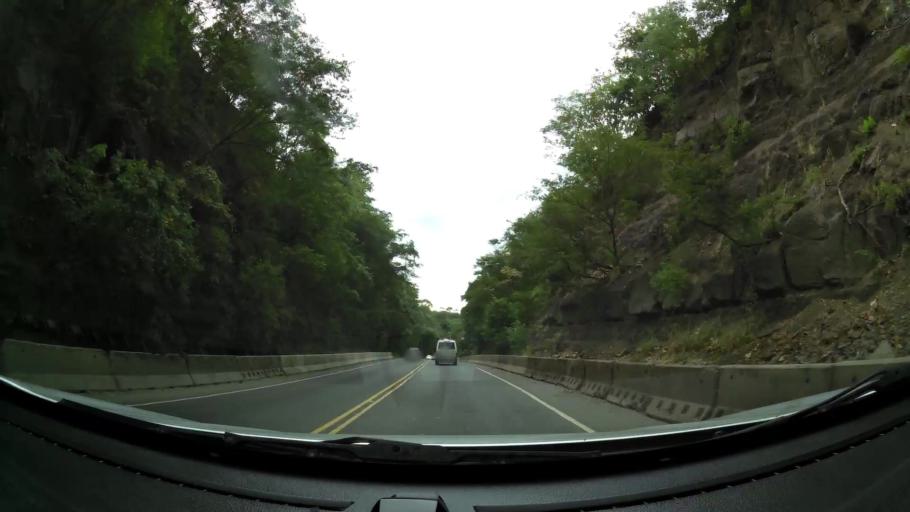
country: CR
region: Puntarenas
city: Esparza
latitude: 9.9179
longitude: -84.7074
